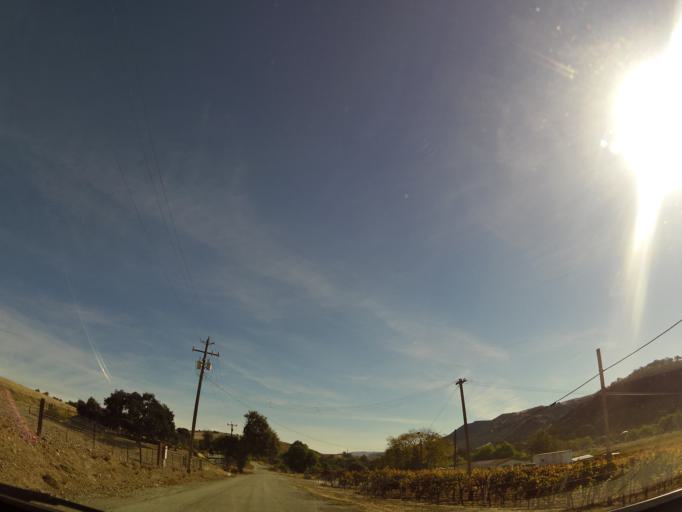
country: US
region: California
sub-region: San Benito County
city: Ridgemark
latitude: 36.7824
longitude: -121.3156
